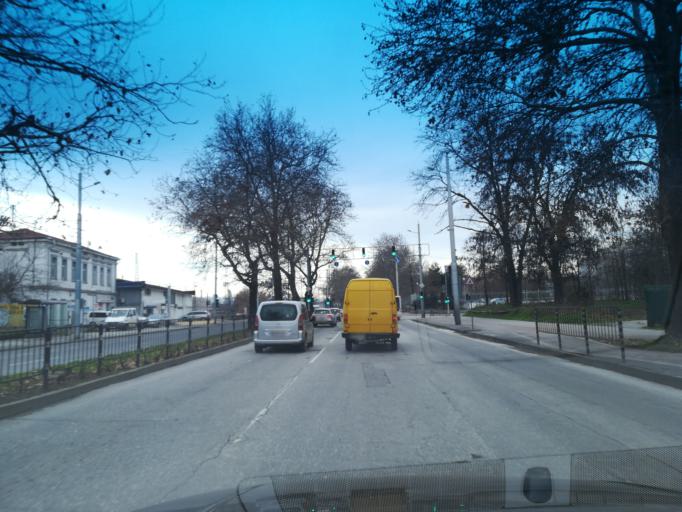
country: BG
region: Plovdiv
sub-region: Obshtina Plovdiv
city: Plovdiv
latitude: 42.1339
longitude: 24.7356
